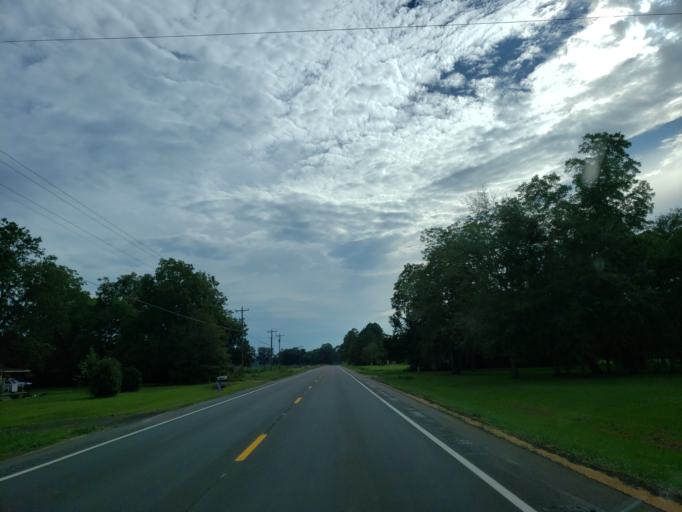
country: US
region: Georgia
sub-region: Irwin County
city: Ocilla
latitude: 31.5816
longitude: -83.2845
